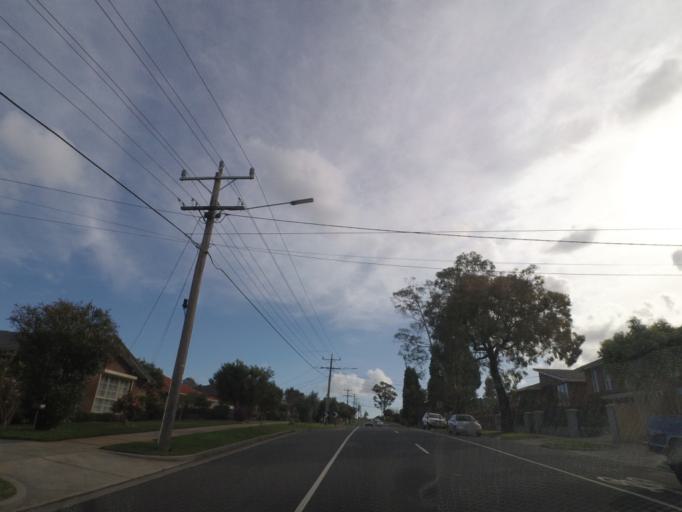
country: AU
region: Victoria
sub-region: Whitehorse
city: Vermont South
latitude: -37.8478
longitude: 145.1829
